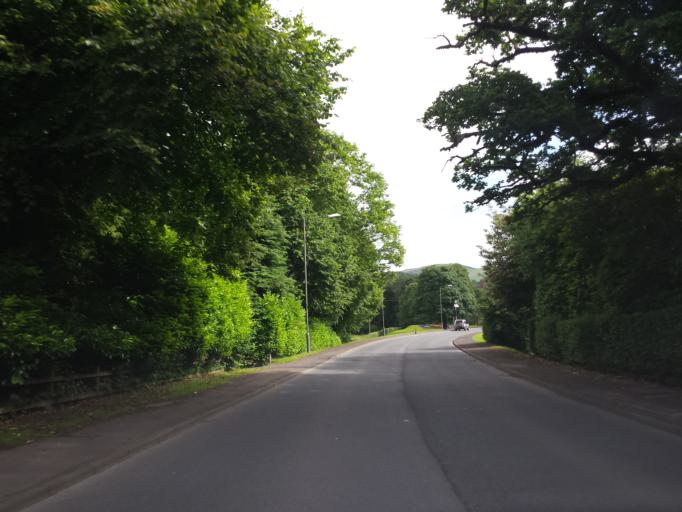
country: GB
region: Scotland
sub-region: Dumfries and Galloway
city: Moffat
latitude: 55.3276
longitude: -3.4472
